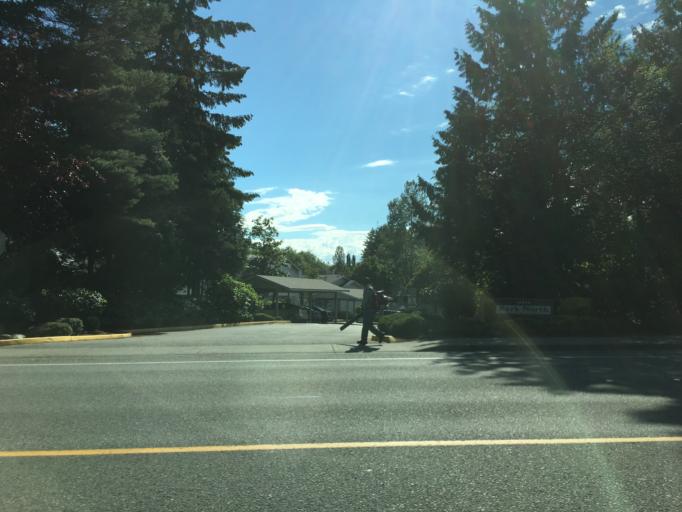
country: US
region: Washington
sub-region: Snohomish County
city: North Creek
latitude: 47.8264
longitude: -122.2081
